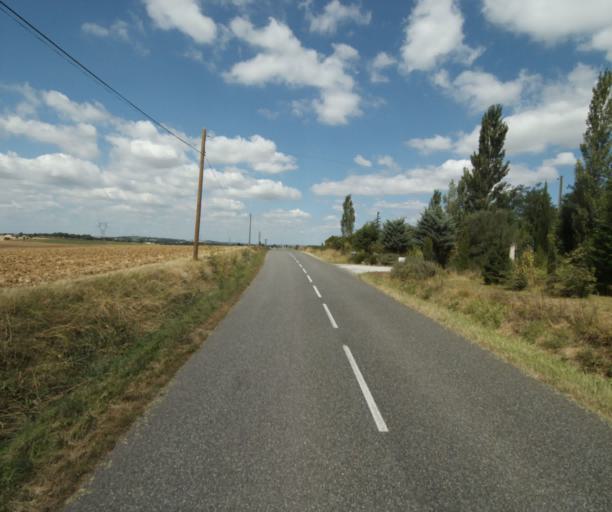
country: FR
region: Midi-Pyrenees
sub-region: Departement de la Haute-Garonne
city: Saint-Felix-Lauragais
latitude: 43.4624
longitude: 1.8292
